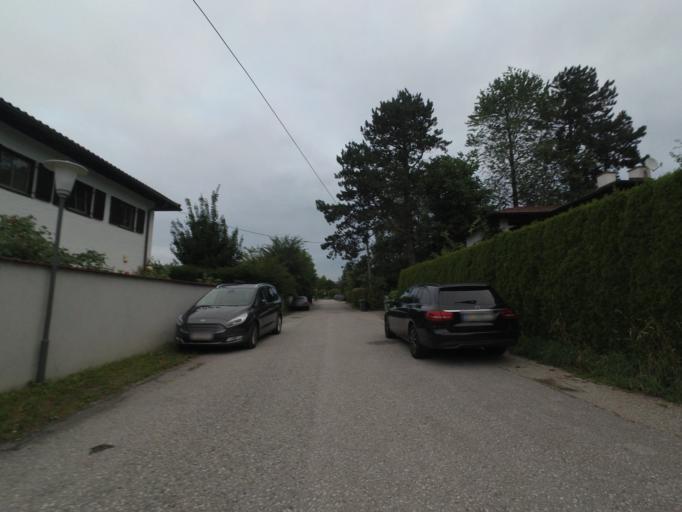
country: AT
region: Salzburg
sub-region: Politischer Bezirk Salzburg-Umgebung
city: Anif
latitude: 47.7709
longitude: 13.0513
